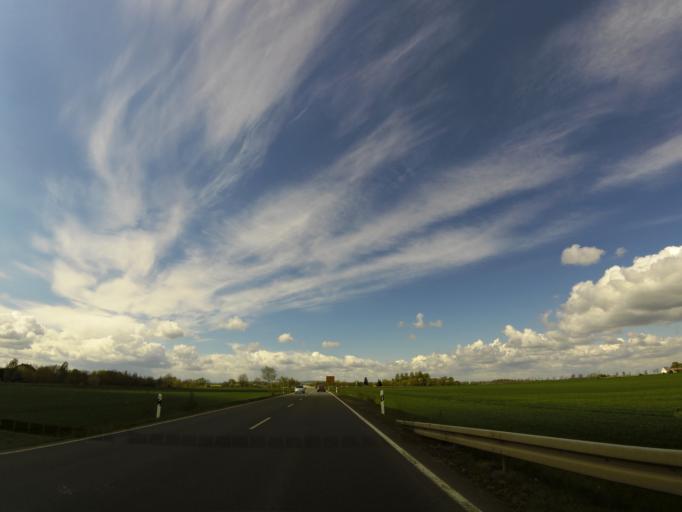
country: DE
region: Saxony-Anhalt
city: Groeningen
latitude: 51.9459
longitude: 11.2180
